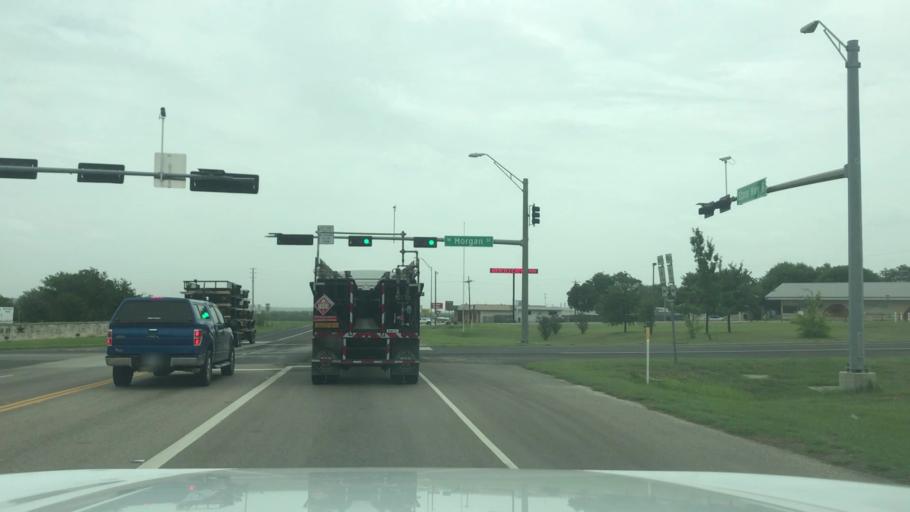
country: US
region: Texas
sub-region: Bosque County
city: Meridian
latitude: 31.9156
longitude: -97.6657
